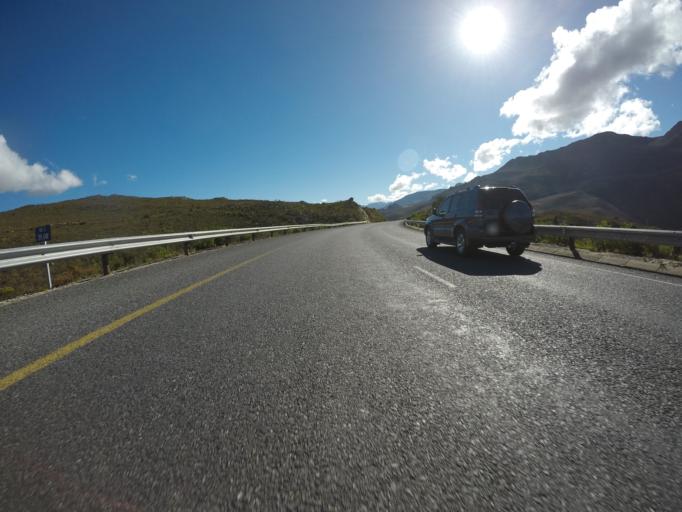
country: ZA
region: Western Cape
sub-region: Overberg District Municipality
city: Grabouw
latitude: -34.2163
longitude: 19.1702
